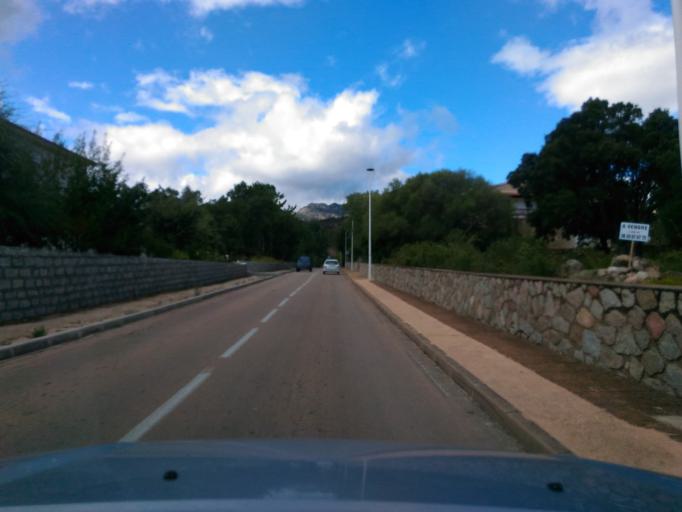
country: FR
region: Corsica
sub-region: Departement de la Corse-du-Sud
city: Porto-Vecchio
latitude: 41.7005
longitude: 9.3436
